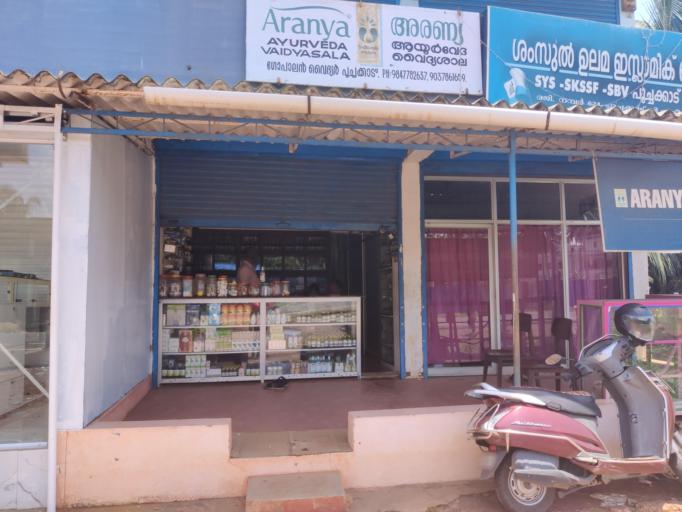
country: IN
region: Kerala
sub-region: Kasaragod District
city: Kannangad
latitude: 12.3791
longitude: 75.0512
